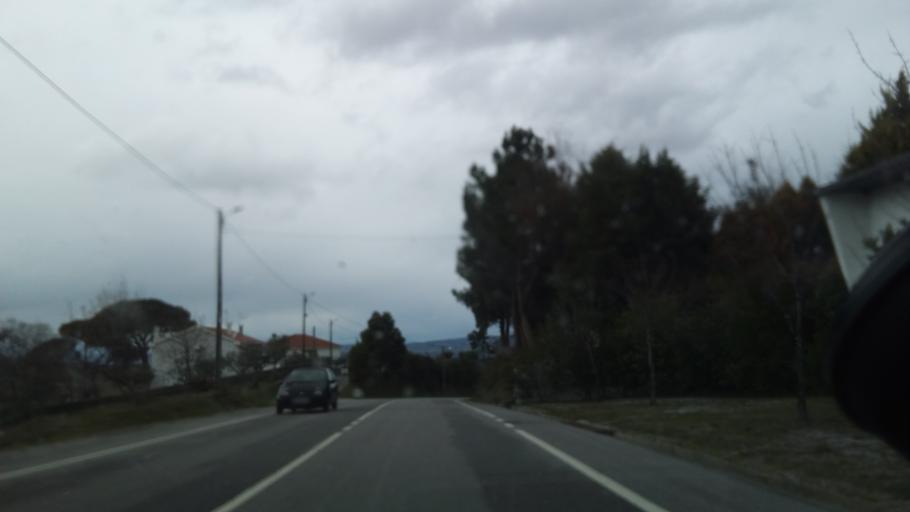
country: PT
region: Guarda
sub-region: Manteigas
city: Manteigas
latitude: 40.5046
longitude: -7.5844
